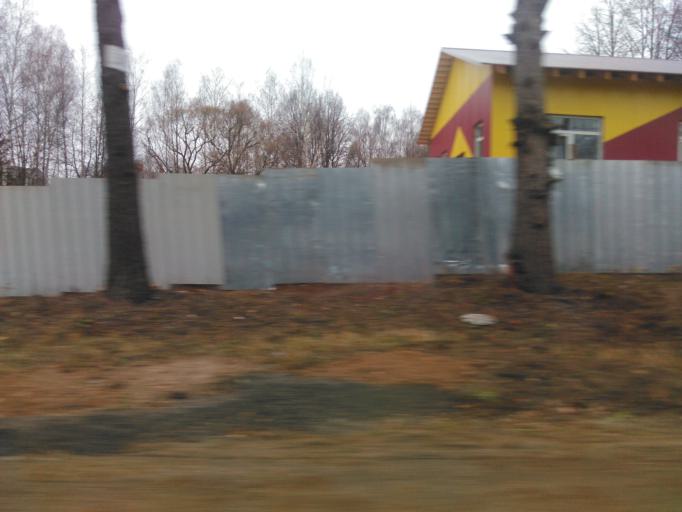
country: RU
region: Moskovskaya
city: Ashukino
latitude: 56.1283
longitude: 37.9755
